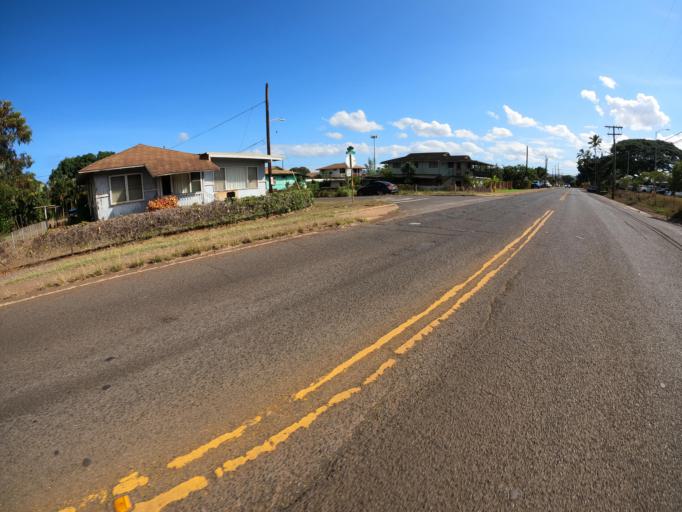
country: US
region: Hawaii
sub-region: Honolulu County
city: Waialua
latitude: 21.5674
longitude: -158.1274
